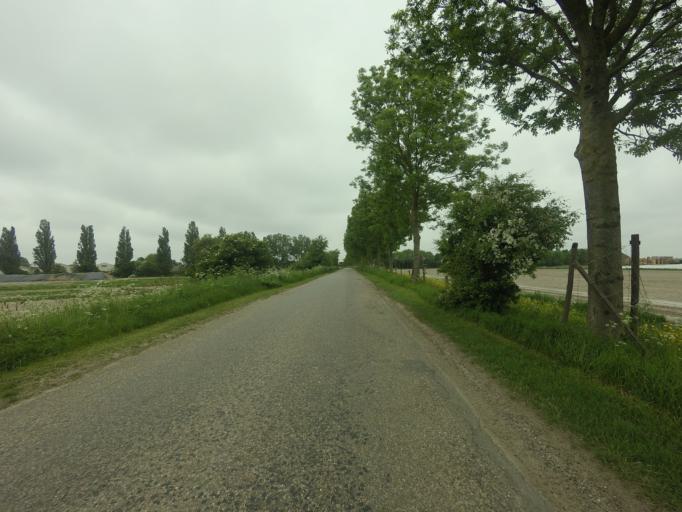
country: NL
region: South Holland
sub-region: Gemeente Goeree-Overflakkee
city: Middelharnis
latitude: 51.7194
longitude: 4.1803
